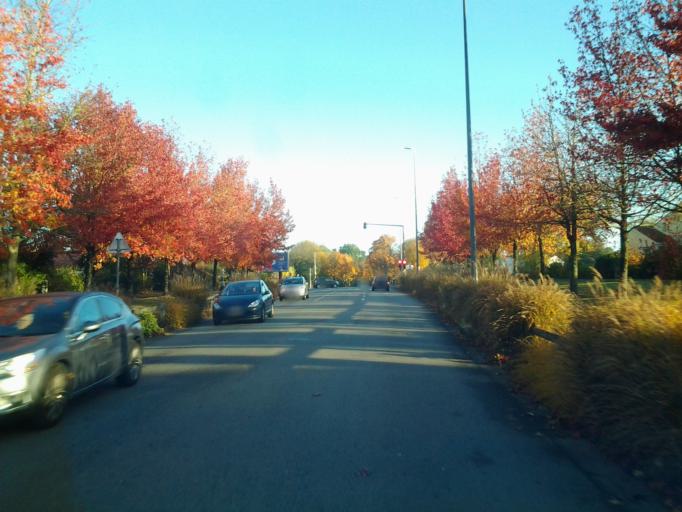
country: FR
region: Pays de la Loire
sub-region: Departement de la Vendee
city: La Roche-sur-Yon
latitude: 46.6631
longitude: -1.4114
